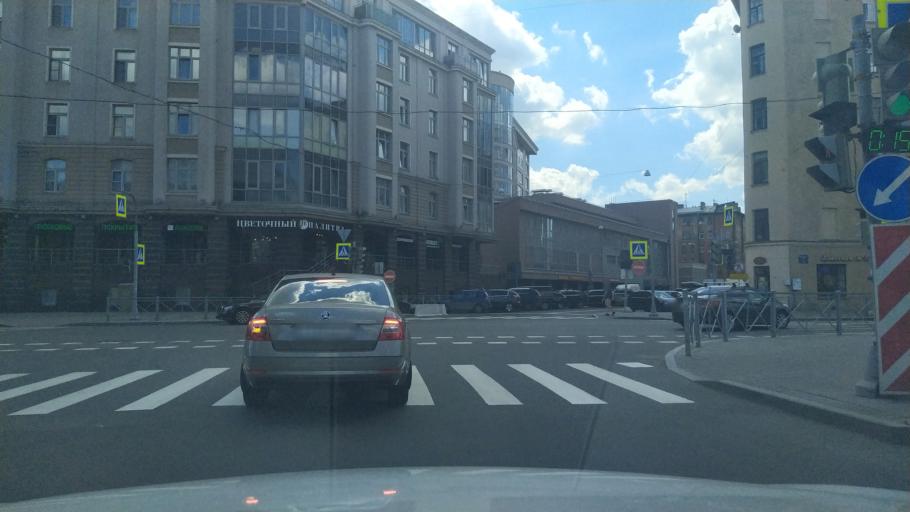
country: RU
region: St.-Petersburg
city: Novaya Derevnya
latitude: 59.9665
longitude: 30.2887
